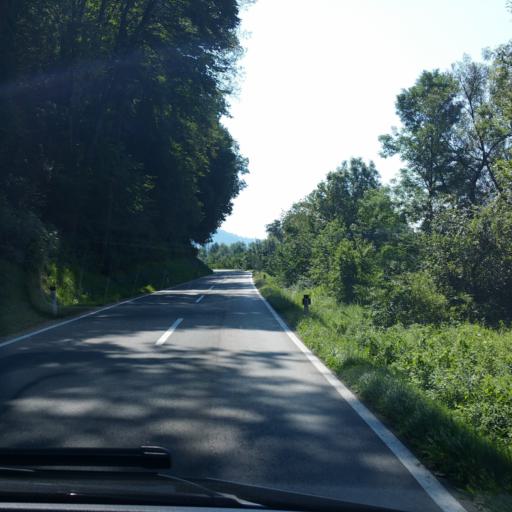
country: AT
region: Styria
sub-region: Politischer Bezirk Leibnitz
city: Kitzeck im Sausal
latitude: 46.7601
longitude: 15.4127
